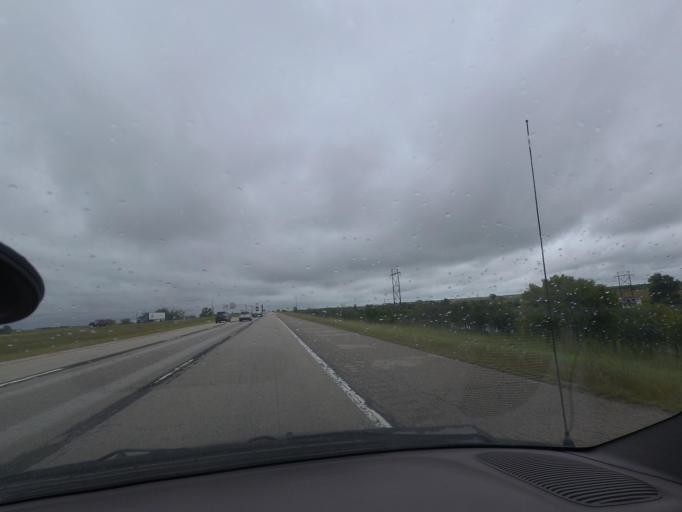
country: US
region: Illinois
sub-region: Macon County
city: Harristown
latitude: 39.8482
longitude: -89.0458
